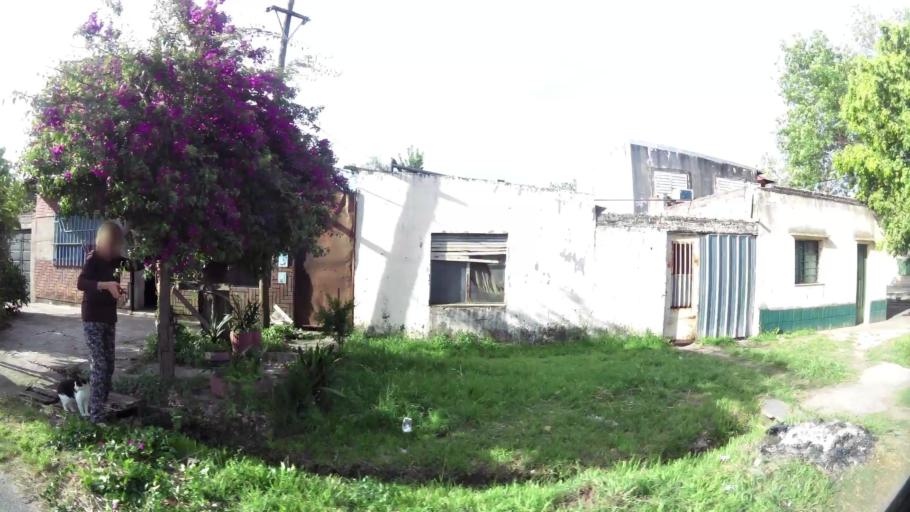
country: AR
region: Santa Fe
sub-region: Departamento de Rosario
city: Rosario
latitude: -32.9760
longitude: -60.6872
